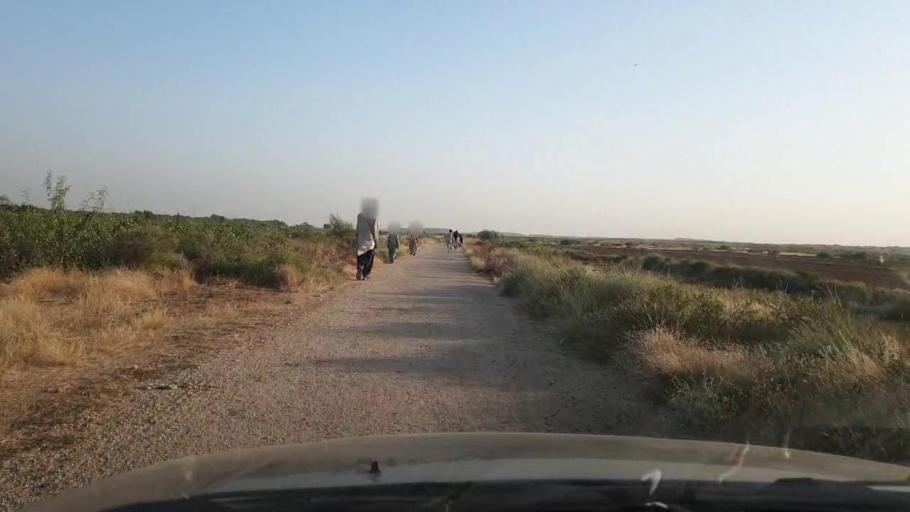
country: PK
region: Sindh
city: Kotri
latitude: 25.2302
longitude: 68.2244
